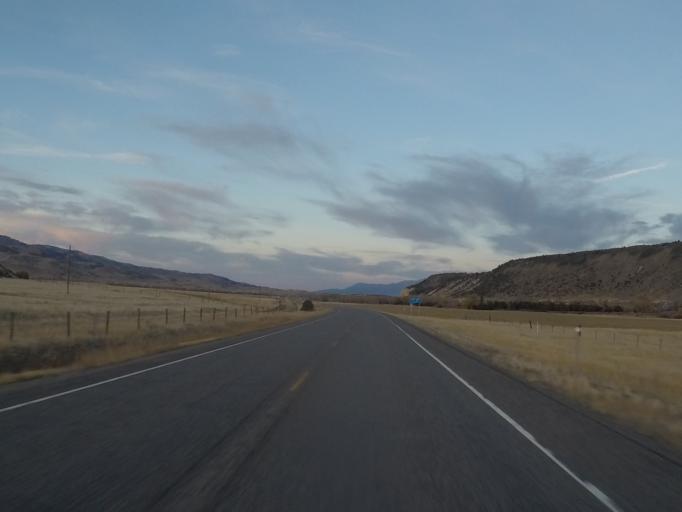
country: US
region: Montana
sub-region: Gallatin County
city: Bozeman
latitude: 45.2828
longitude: -110.8480
